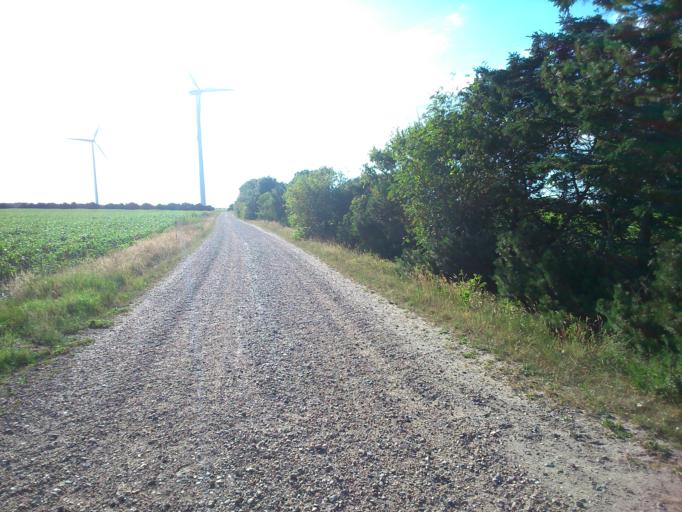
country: DK
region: Central Jutland
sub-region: Ringkobing-Skjern Kommune
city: Skjern
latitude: 55.8602
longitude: 8.3322
